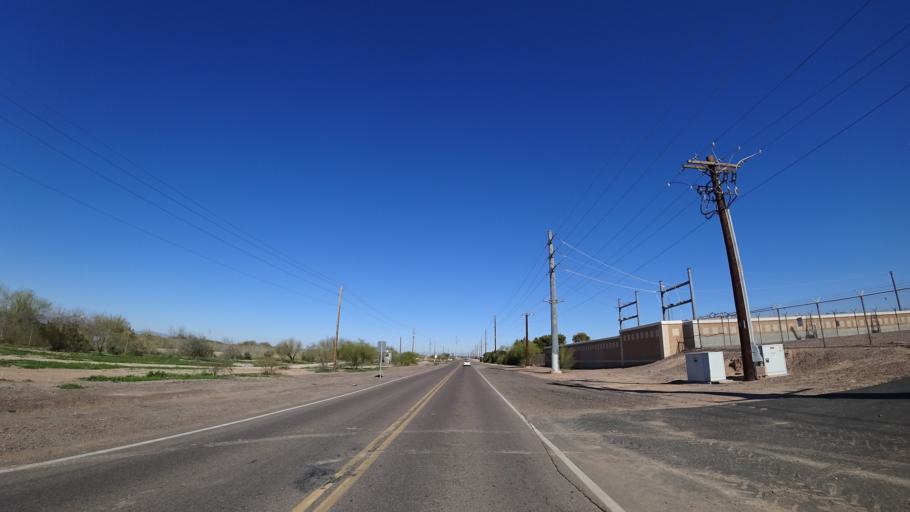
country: US
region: Arizona
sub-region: Maricopa County
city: Tolleson
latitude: 33.3924
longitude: -112.2543
